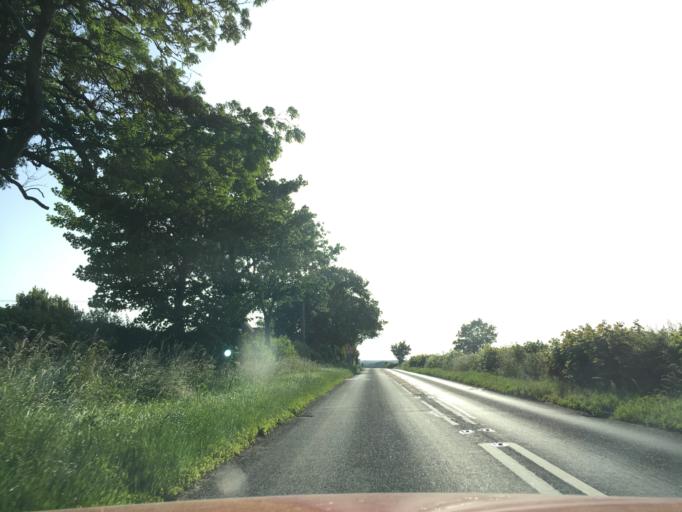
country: GB
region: England
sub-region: Gloucestershire
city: Fairford
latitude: 51.7018
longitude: -1.8249
